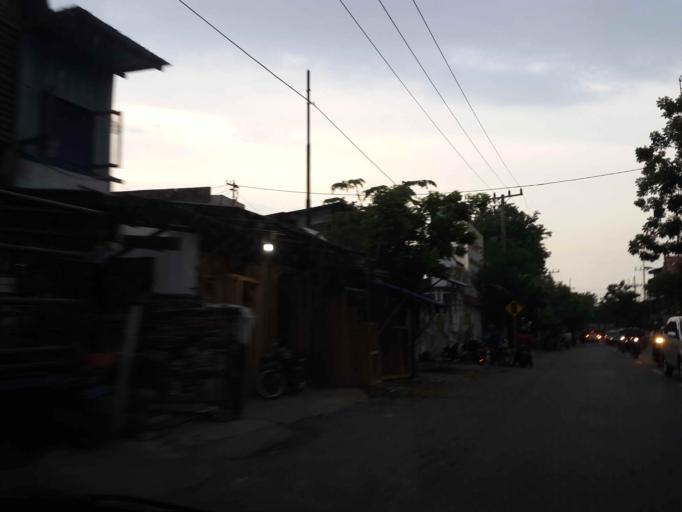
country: ID
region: East Java
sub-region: Kota Surabaya
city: Surabaya
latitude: -7.2529
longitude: 112.7287
